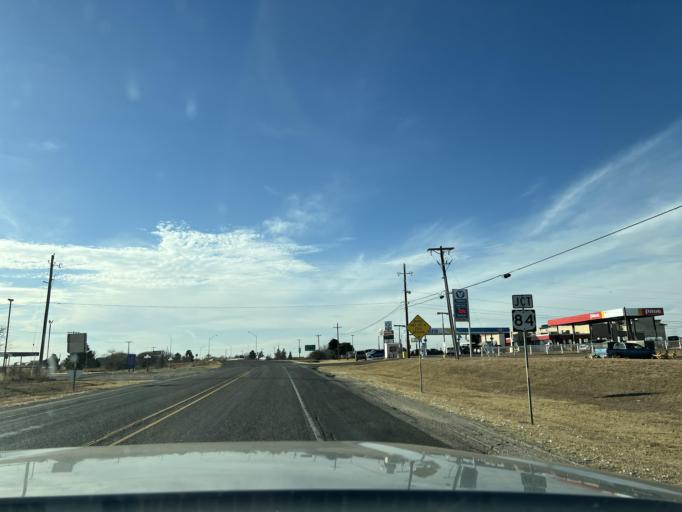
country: US
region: Texas
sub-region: Scurry County
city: Snyder
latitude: 32.7046
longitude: -100.8646
